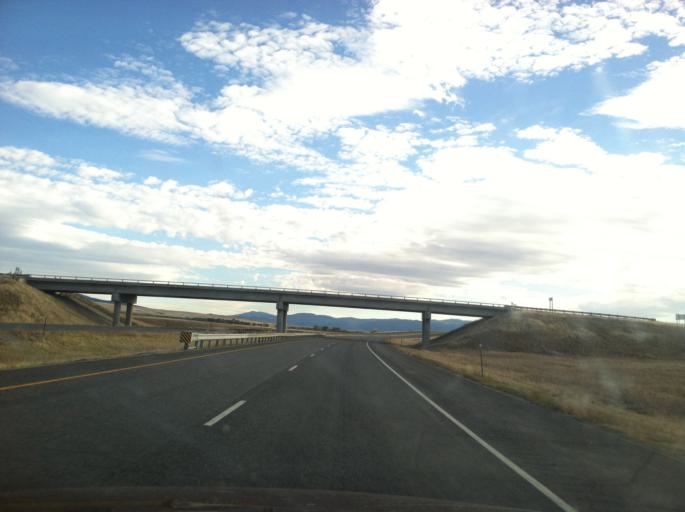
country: US
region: Montana
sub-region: Deer Lodge County
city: Warm Springs
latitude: 46.2714
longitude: -112.7480
